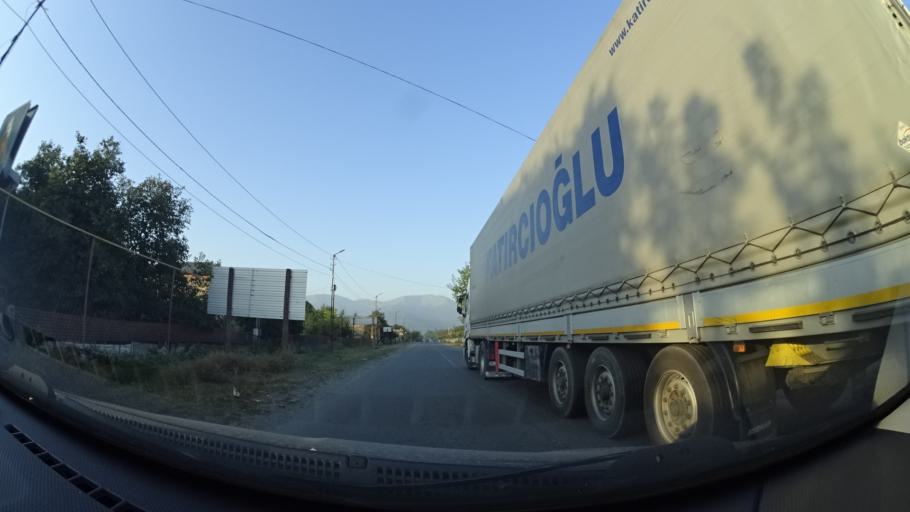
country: GE
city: Bagdadi
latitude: 41.8192
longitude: 46.0662
